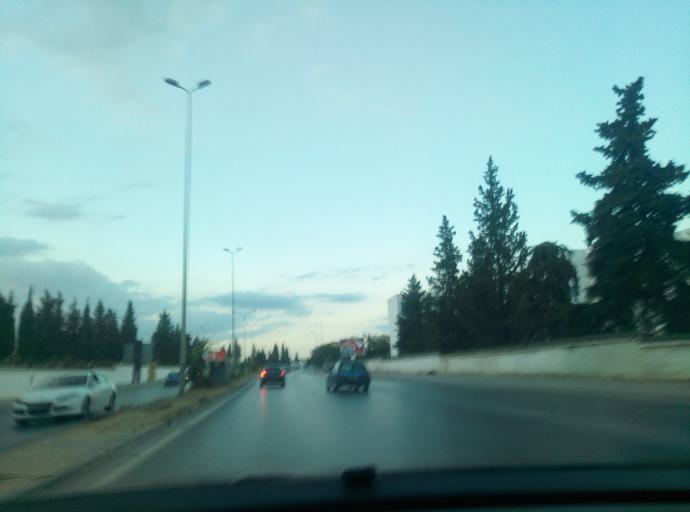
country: TN
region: Manouba
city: Manouba
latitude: 36.8127
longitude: 10.1206
